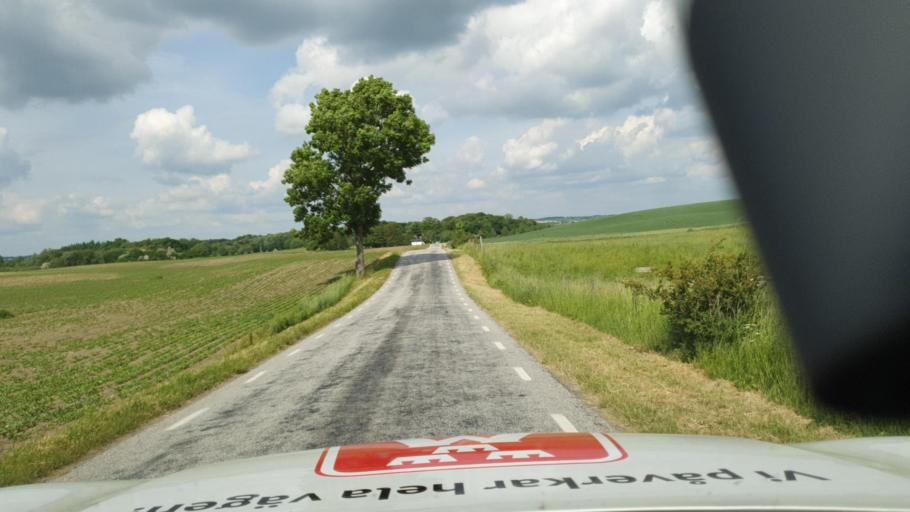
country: SE
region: Skane
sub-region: Skurups Kommun
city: Skurup
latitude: 55.5055
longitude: 13.4881
